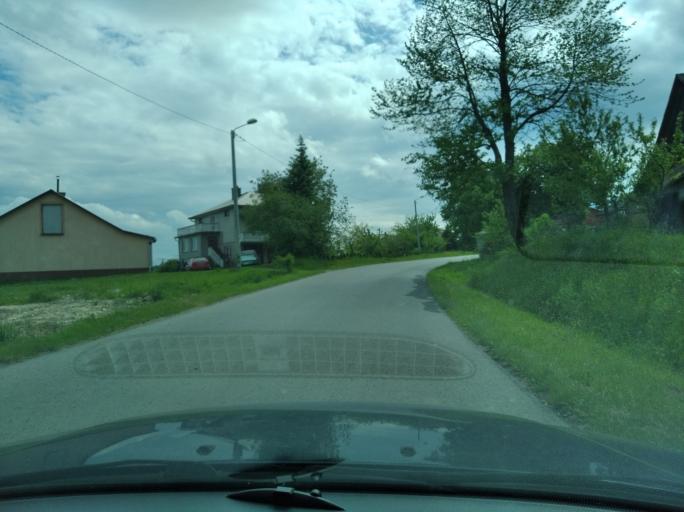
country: PL
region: Subcarpathian Voivodeship
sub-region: Powiat ropczycko-sedziszowski
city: Ropczyce
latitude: 50.0032
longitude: 21.6140
